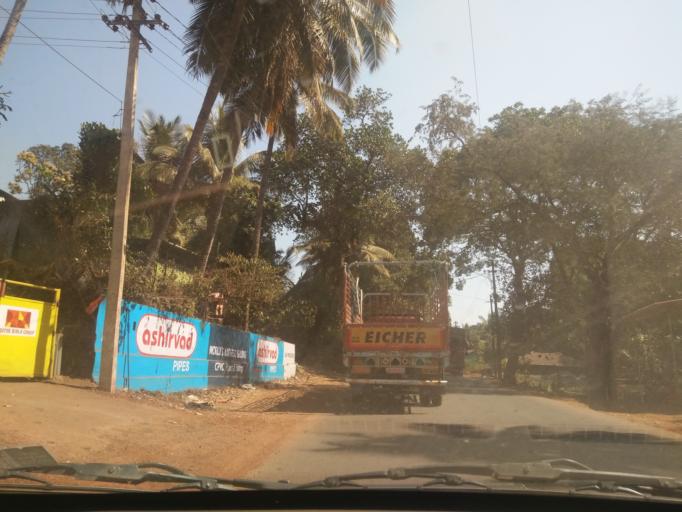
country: IN
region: Goa
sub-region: North Goa
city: Aldona
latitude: 15.6198
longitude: 73.9069
